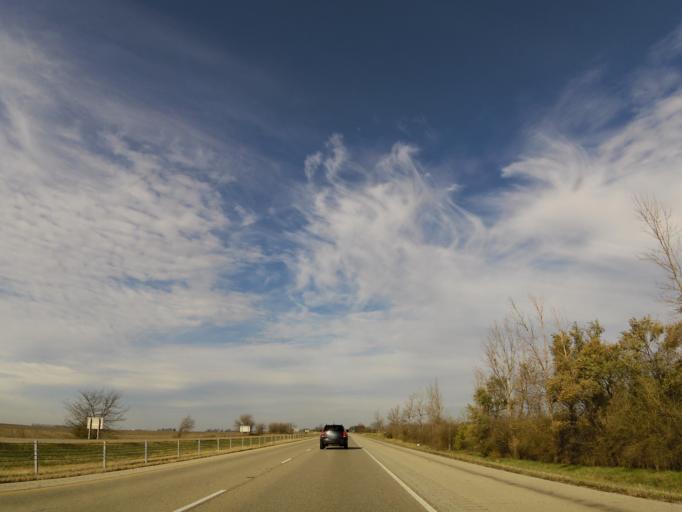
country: US
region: Illinois
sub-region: McLean County
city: Danvers
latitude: 40.5692
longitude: -89.1231
